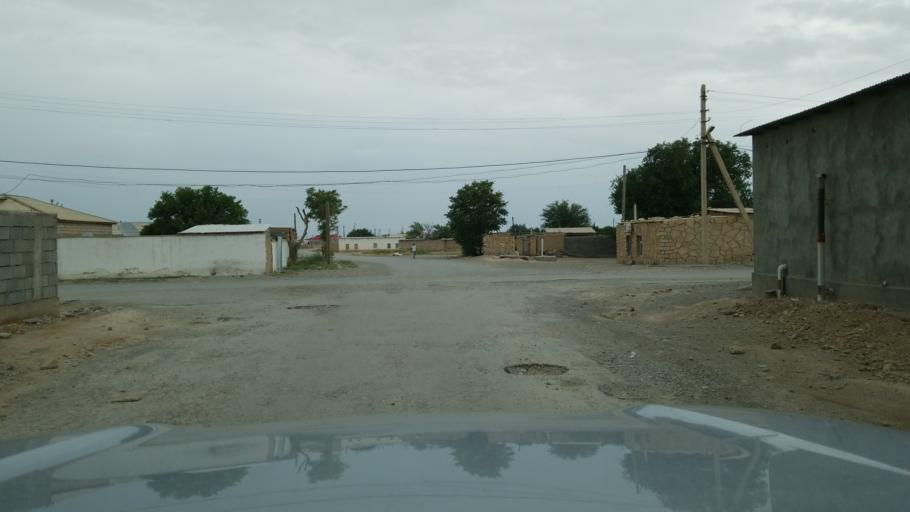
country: TM
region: Balkan
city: Serdar
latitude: 38.9883
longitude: 56.2772
